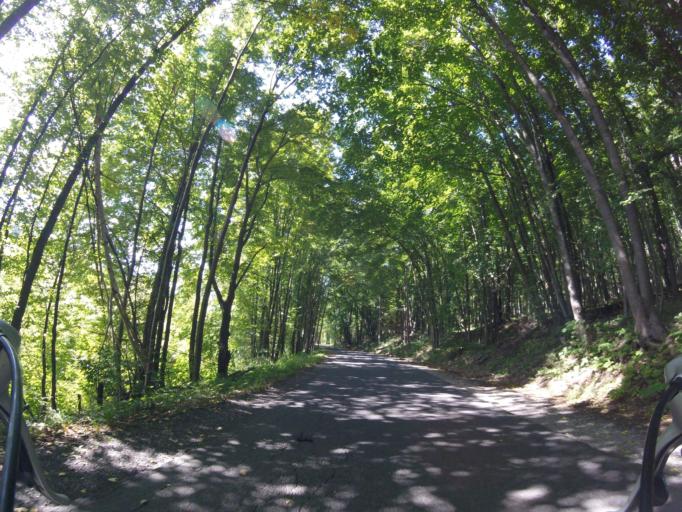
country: HU
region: Borsod-Abauj-Zemplen
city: Kazincbarcika
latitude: 48.1041
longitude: 20.5690
